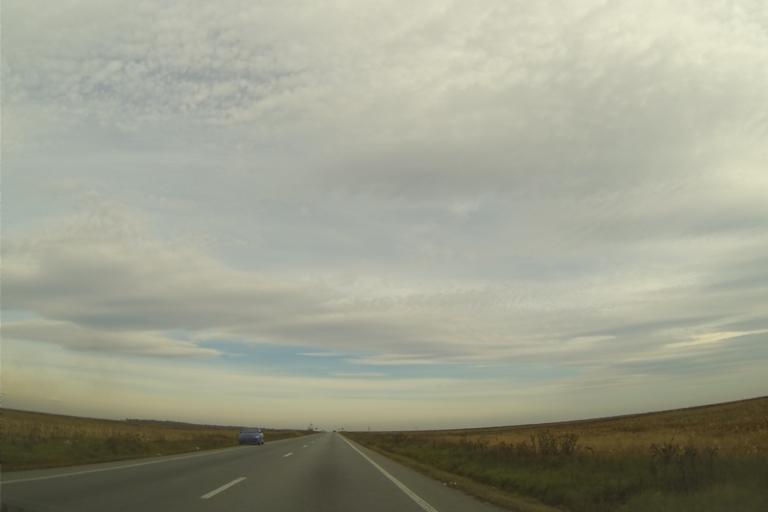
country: RO
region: Olt
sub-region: Comuna Priseaca
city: Priseaca
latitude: 44.4955
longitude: 24.4547
